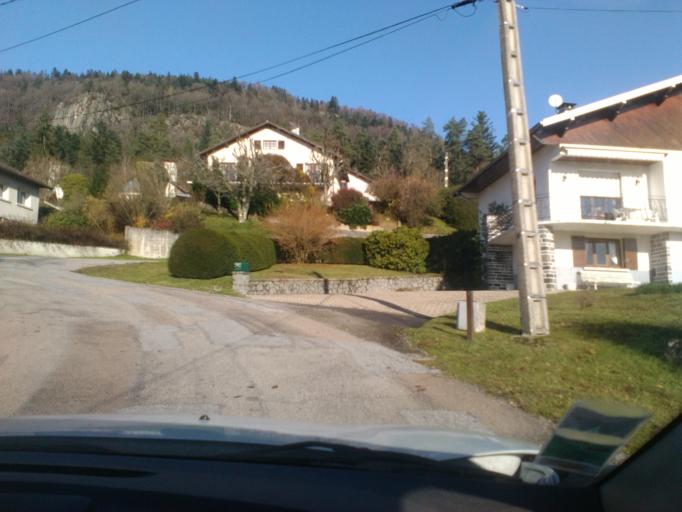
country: FR
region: Lorraine
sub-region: Departement des Vosges
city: Saint-Ame
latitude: 48.0261
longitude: 6.6587
